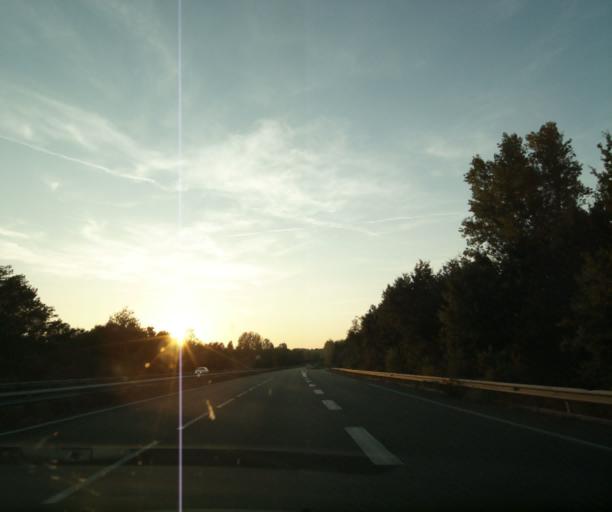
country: FR
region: Aquitaine
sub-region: Departement du Lot-et-Garonne
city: Fourques-sur-Garonne
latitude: 44.4290
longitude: 0.1406
